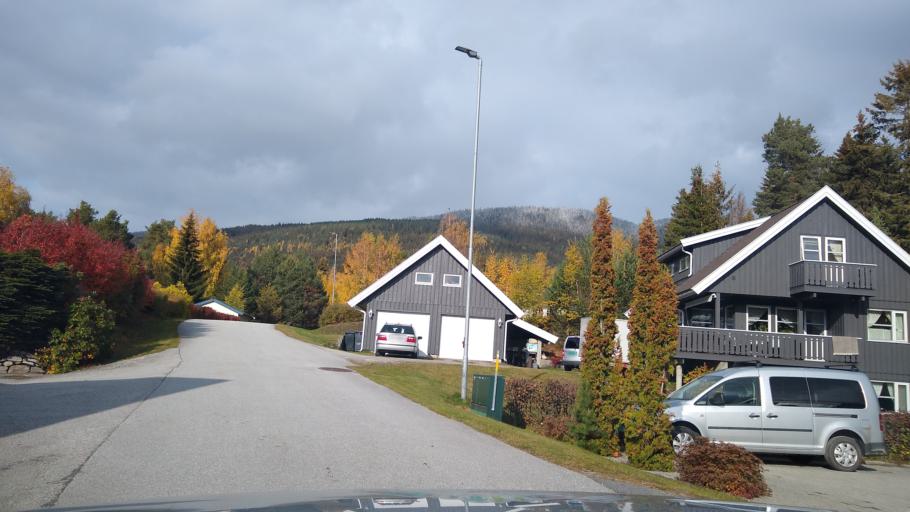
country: NO
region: Oppland
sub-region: Ringebu
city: Ringebu
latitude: 61.5402
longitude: 10.1363
